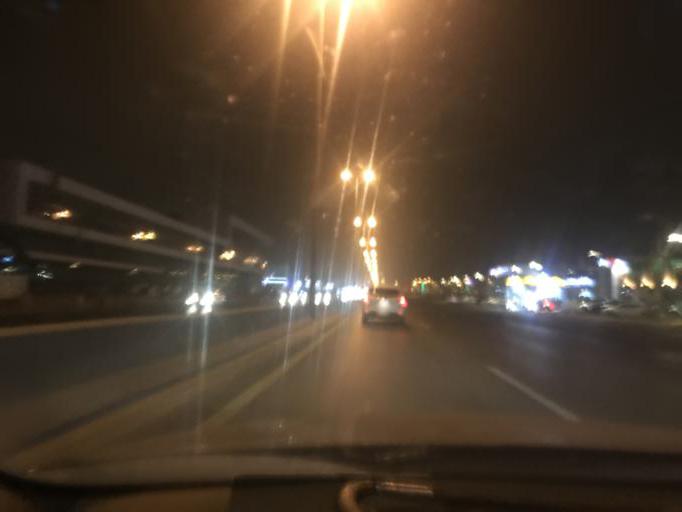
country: SA
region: Ar Riyad
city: Riyadh
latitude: 24.8339
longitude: 46.7348
